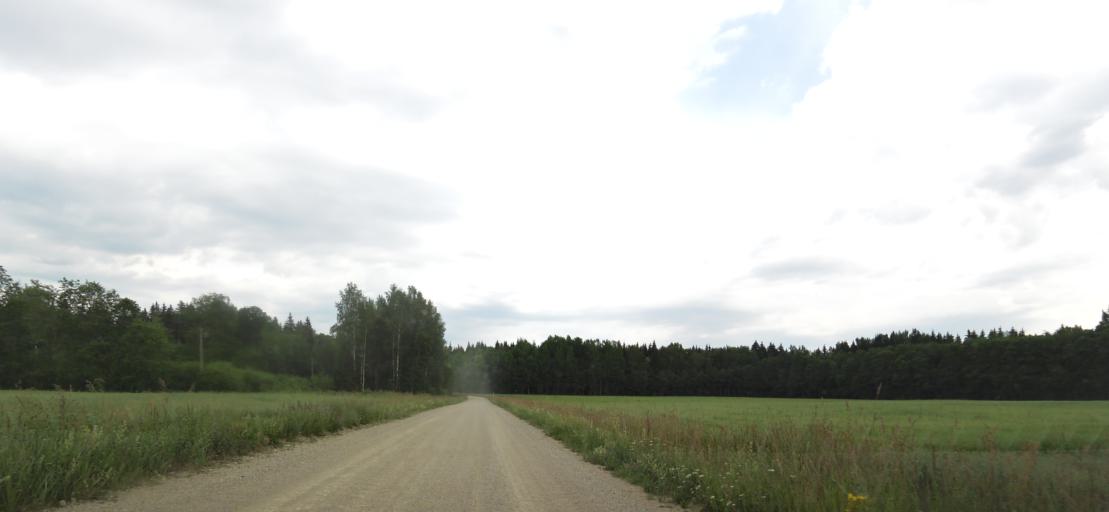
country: LT
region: Panevezys
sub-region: Birzai
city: Birzai
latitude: 56.2971
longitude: 24.9607
